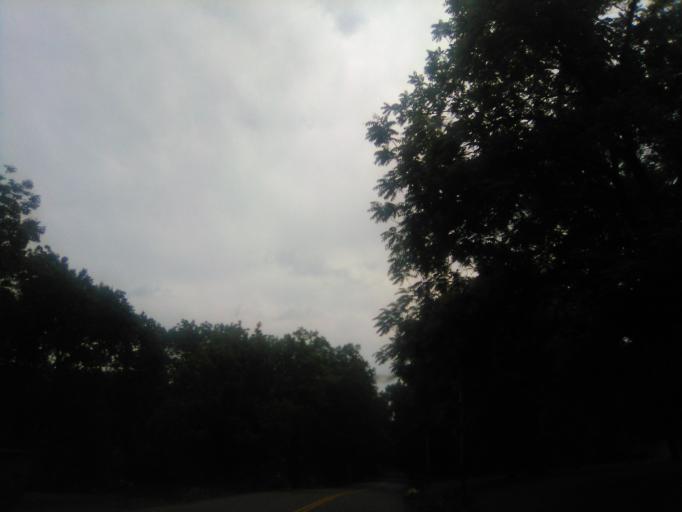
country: US
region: Tennessee
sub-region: Davidson County
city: Belle Meade
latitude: 36.1085
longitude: -86.8917
